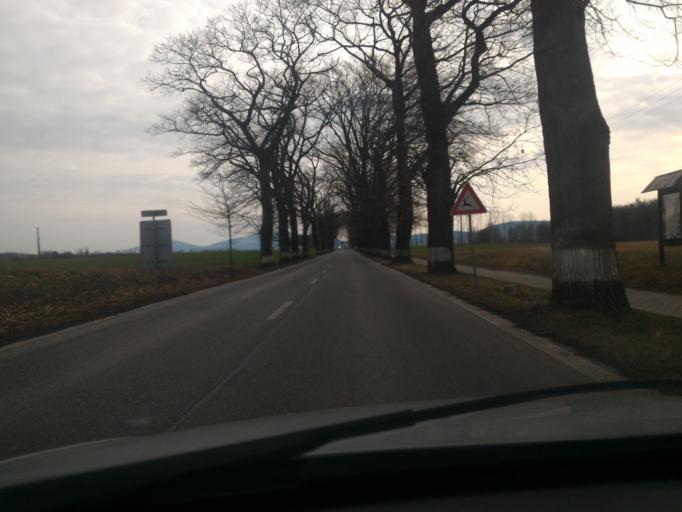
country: CZ
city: Hradek nad Nisou
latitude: 50.8706
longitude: 14.8294
